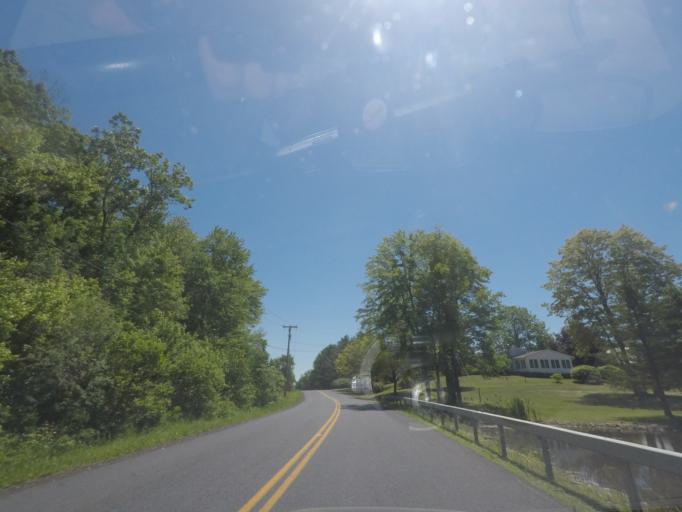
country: US
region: New York
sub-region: Saratoga County
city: Mechanicville
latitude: 42.9411
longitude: -73.7034
